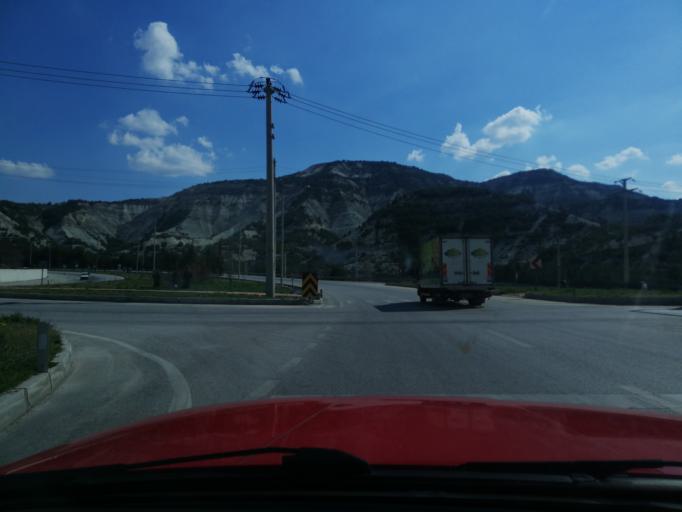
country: TR
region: Burdur
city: Burdur
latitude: 37.7109
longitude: 30.2948
